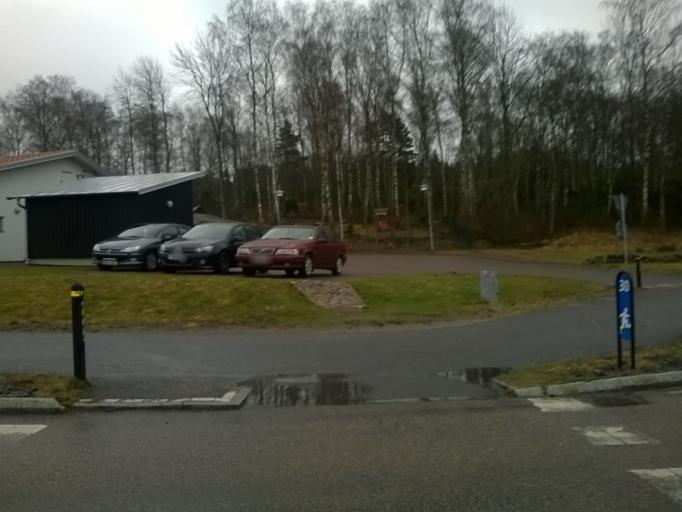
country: SE
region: Vaestra Goetaland
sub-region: Kungalvs Kommun
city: Kungalv
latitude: 57.8941
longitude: 11.9504
